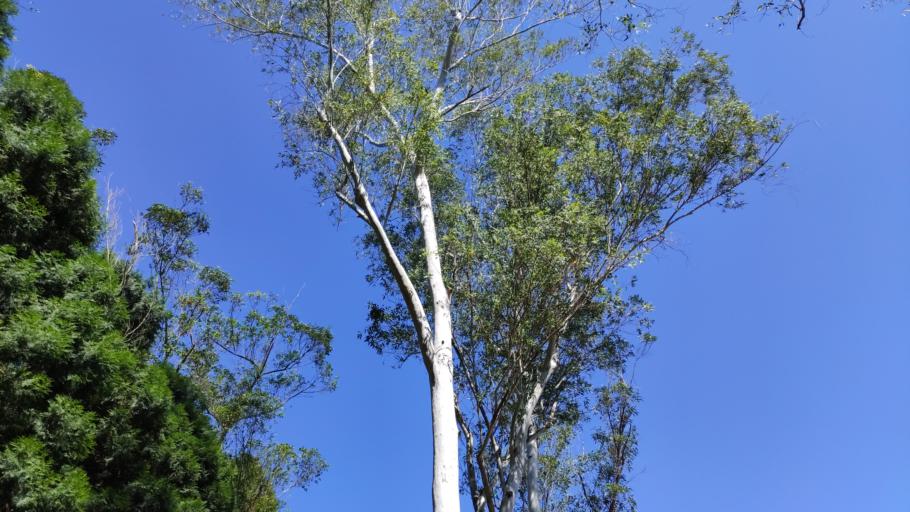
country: TW
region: Taiwan
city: Daxi
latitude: 24.8447
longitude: 121.3014
